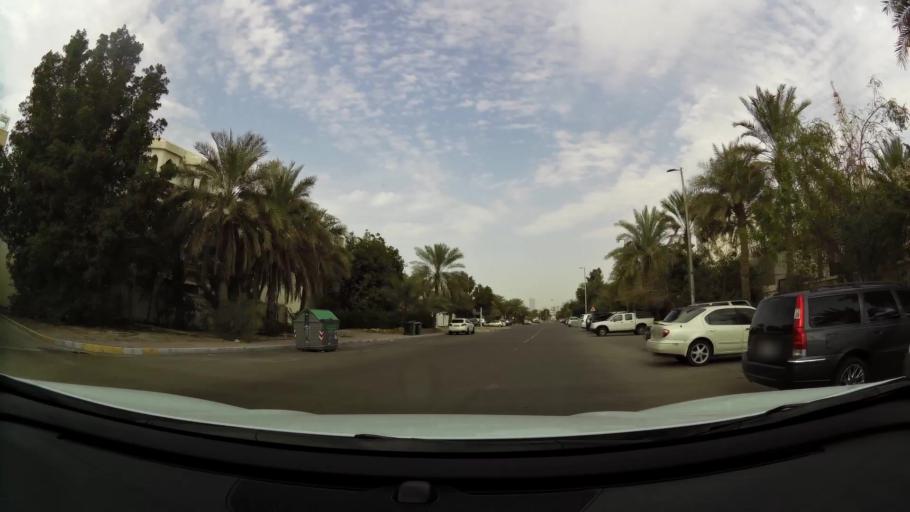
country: AE
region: Abu Dhabi
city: Abu Dhabi
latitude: 24.4603
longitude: 54.3525
